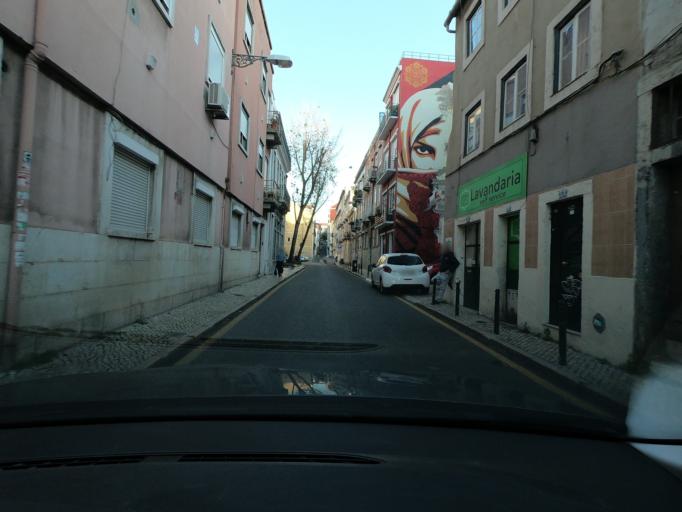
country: PT
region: Lisbon
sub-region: Lisbon
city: Lisbon
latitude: 38.7187
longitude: -9.1279
